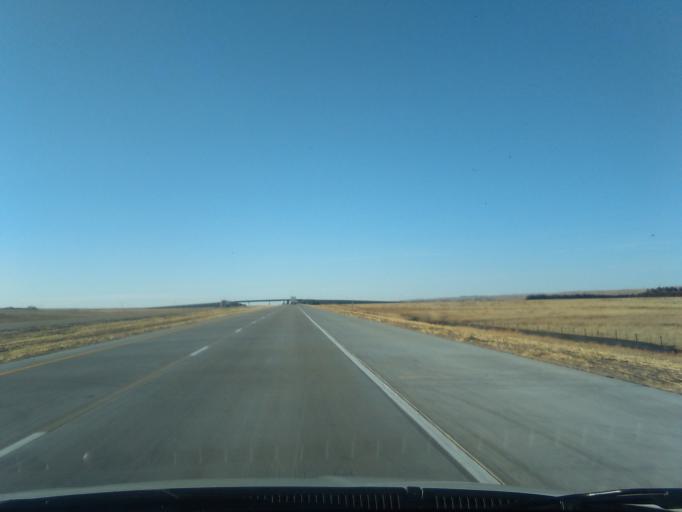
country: US
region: Nebraska
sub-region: Deuel County
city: Chappell
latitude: 41.1041
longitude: -102.5442
